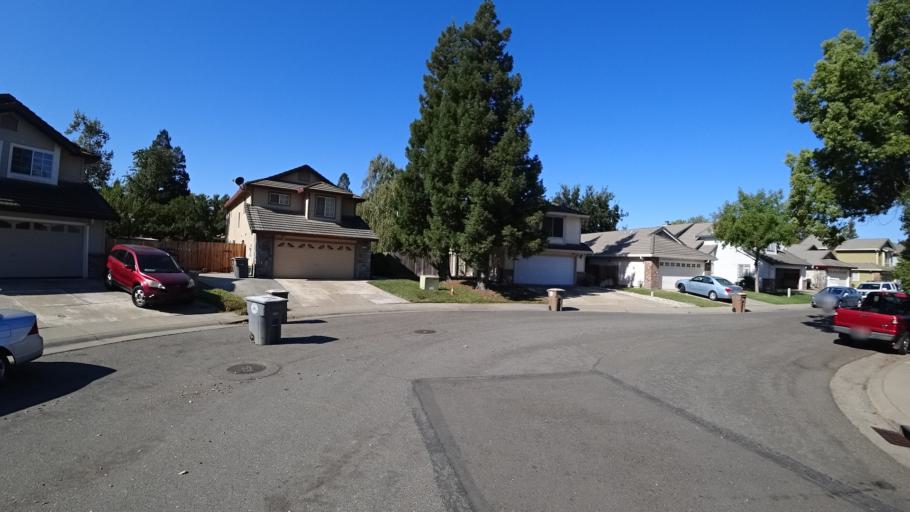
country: US
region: California
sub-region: Sacramento County
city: Laguna
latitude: 38.4354
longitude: -121.4414
